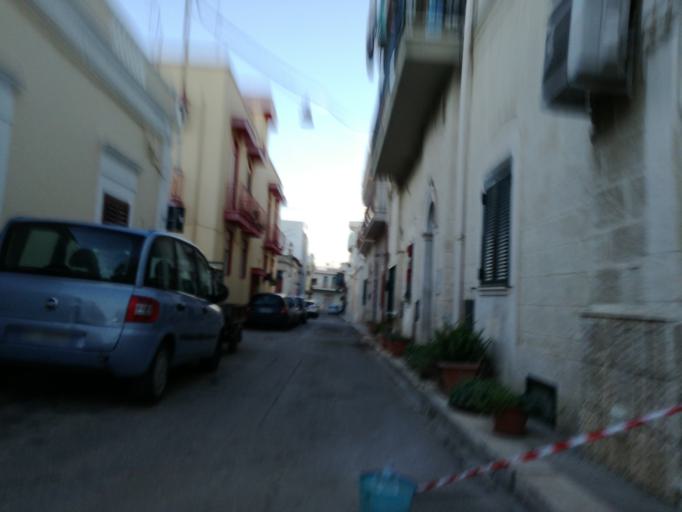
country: IT
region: Apulia
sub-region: Provincia di Bari
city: Adelfia
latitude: 41.0028
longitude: 16.8789
